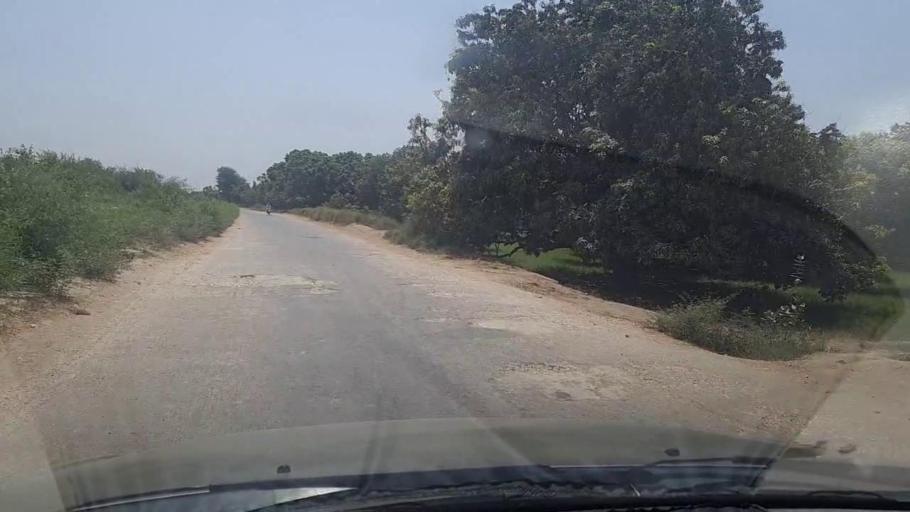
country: PK
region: Sindh
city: Tando Jam
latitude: 25.2902
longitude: 68.5907
